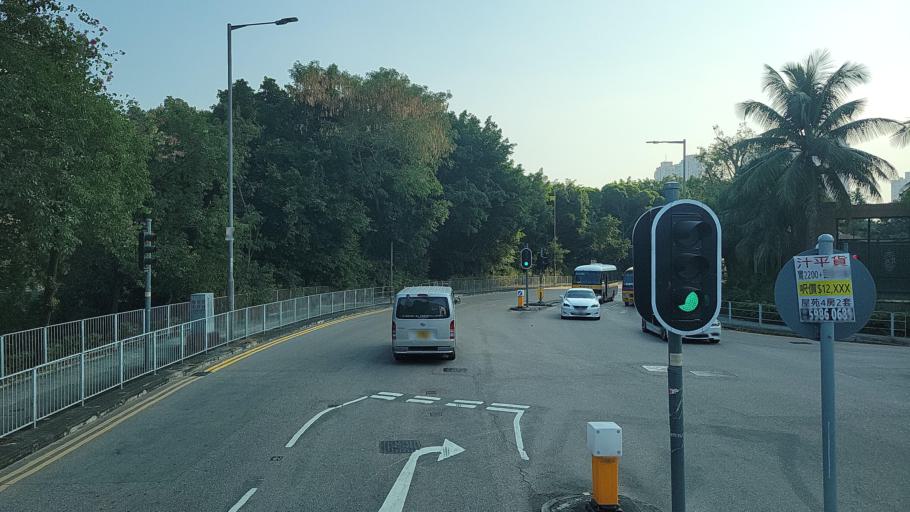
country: HK
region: Tuen Mun
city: Tuen Mun
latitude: 22.3731
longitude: 113.9964
